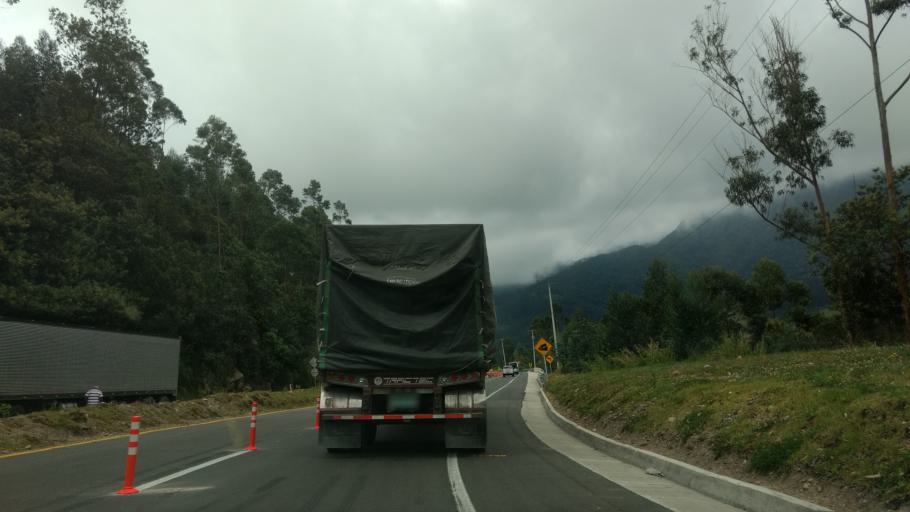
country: CO
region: Cundinamarca
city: El Rosal
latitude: 4.9086
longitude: -74.3021
